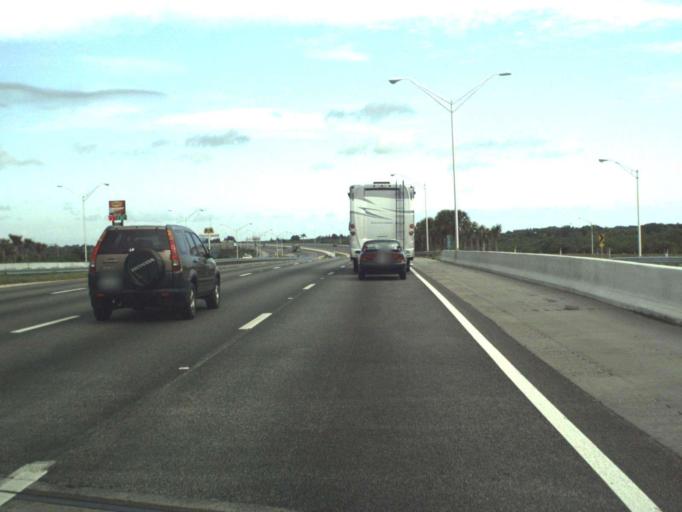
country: US
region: Florida
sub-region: Saint Lucie County
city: Lakewood Park
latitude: 27.4478
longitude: -80.3939
